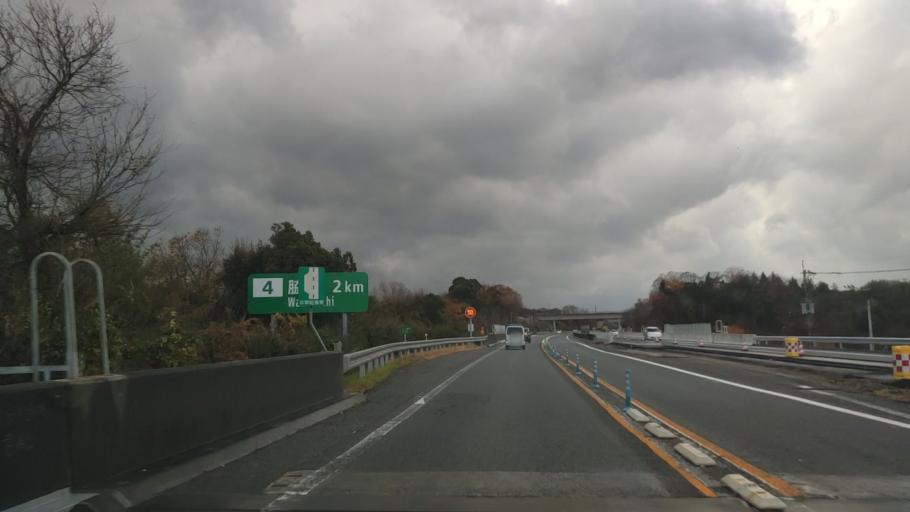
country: JP
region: Tokushima
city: Wakimachi
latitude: 34.0794
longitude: 134.1931
